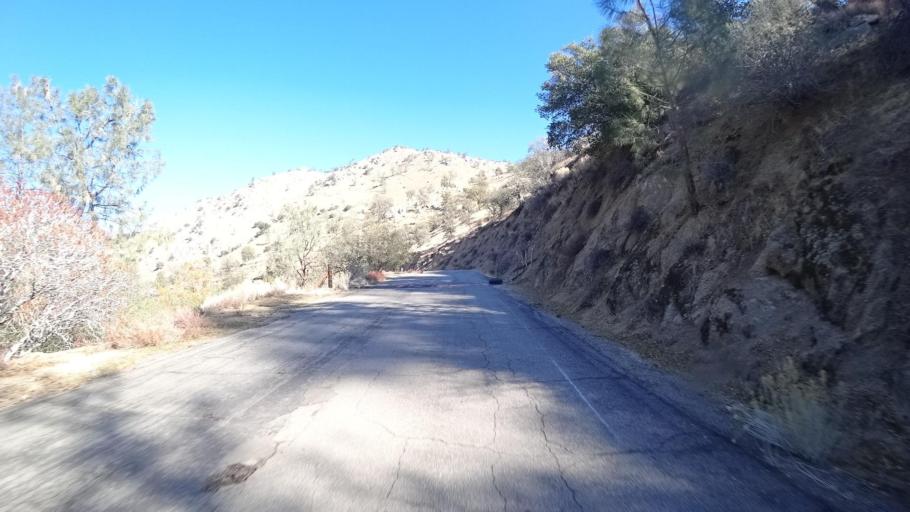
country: US
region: California
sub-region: Kern County
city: Bodfish
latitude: 35.5355
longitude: -118.6156
